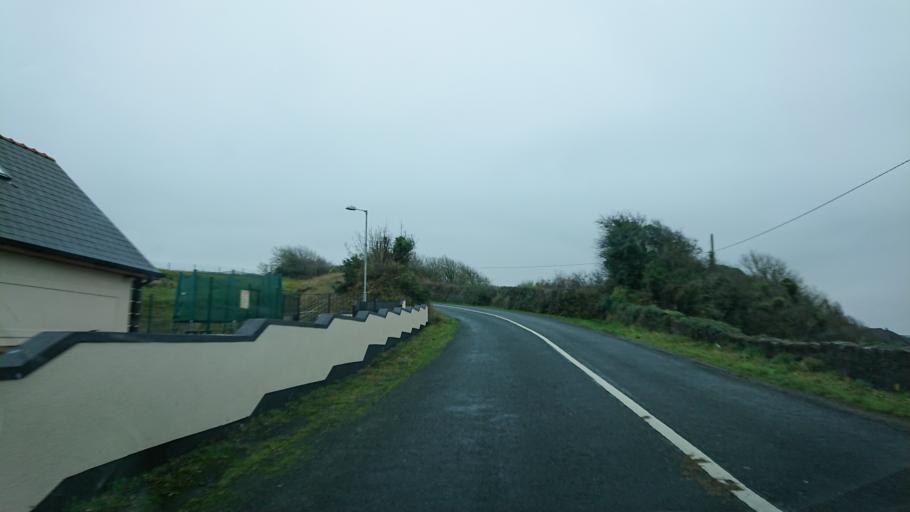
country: IE
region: Munster
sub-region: Waterford
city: Tra Mhor
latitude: 52.1704
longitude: -7.0698
